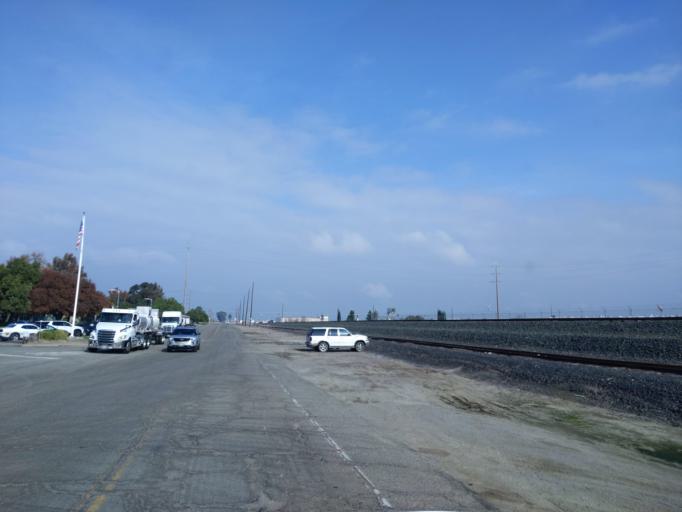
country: US
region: California
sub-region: San Joaquin County
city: Lathrop
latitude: 37.8078
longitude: -121.2754
